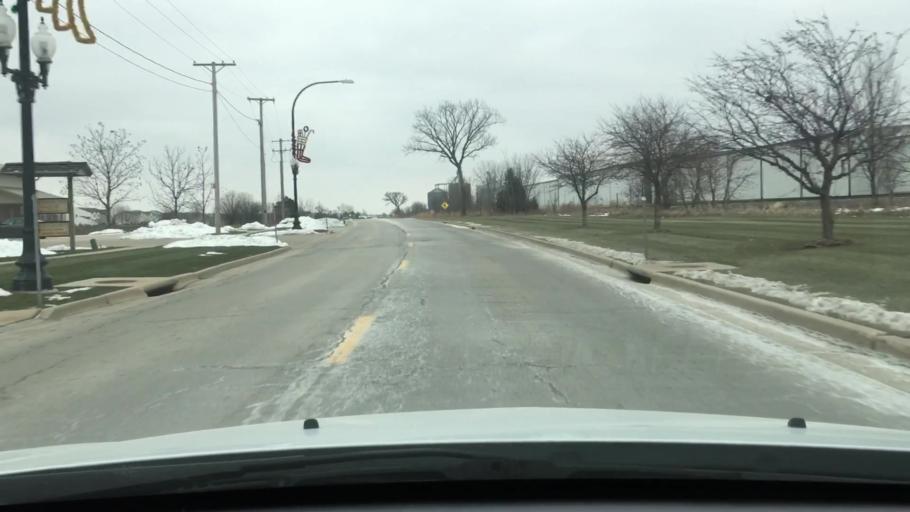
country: US
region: Illinois
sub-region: DeKalb County
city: Waterman
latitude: 41.7691
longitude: -88.7699
